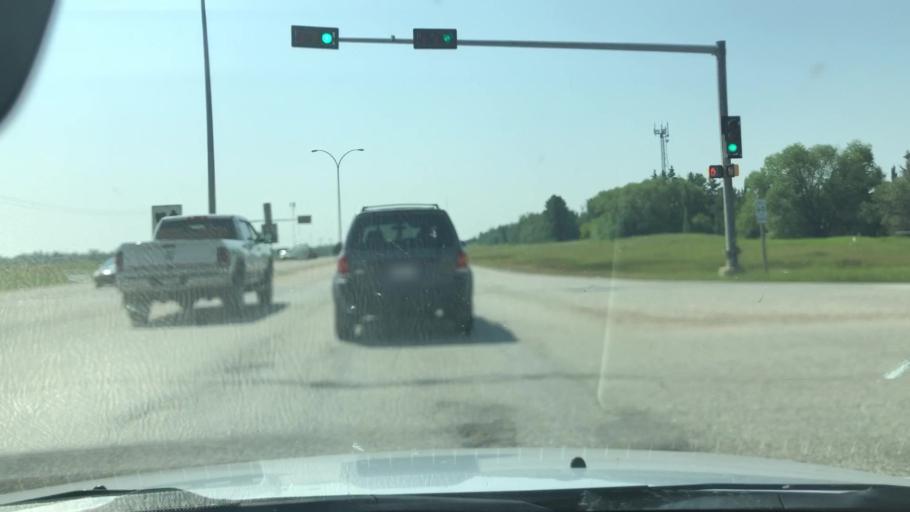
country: CA
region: Alberta
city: Devon
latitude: 53.4541
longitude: -113.7626
